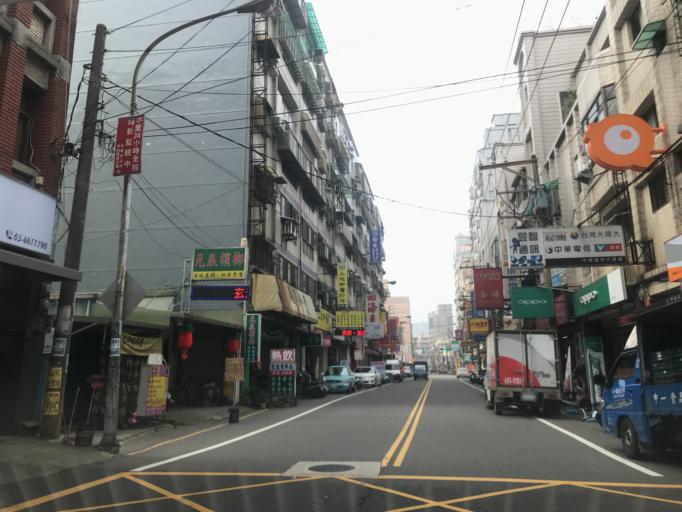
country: TW
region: Taiwan
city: Taoyuan City
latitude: 24.9684
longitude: 121.2341
